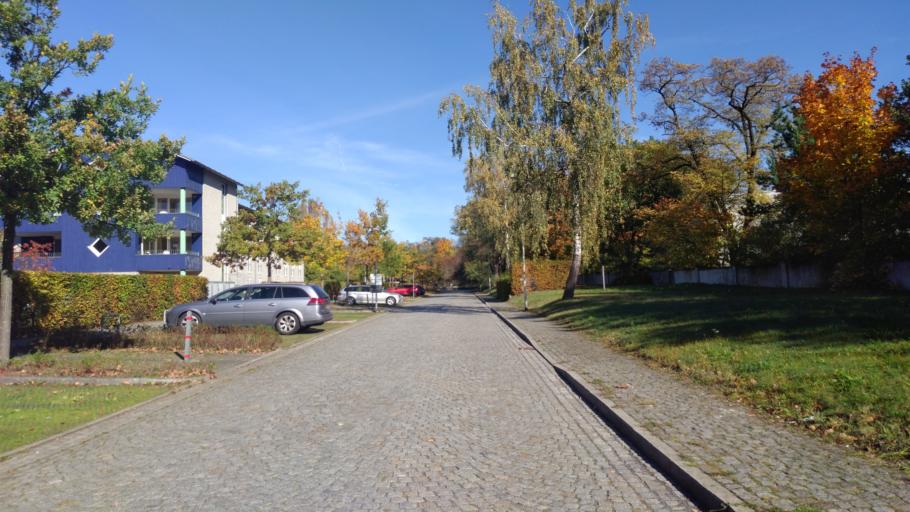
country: DE
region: Saxony
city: Albertstadt
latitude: 51.0981
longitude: 13.7276
